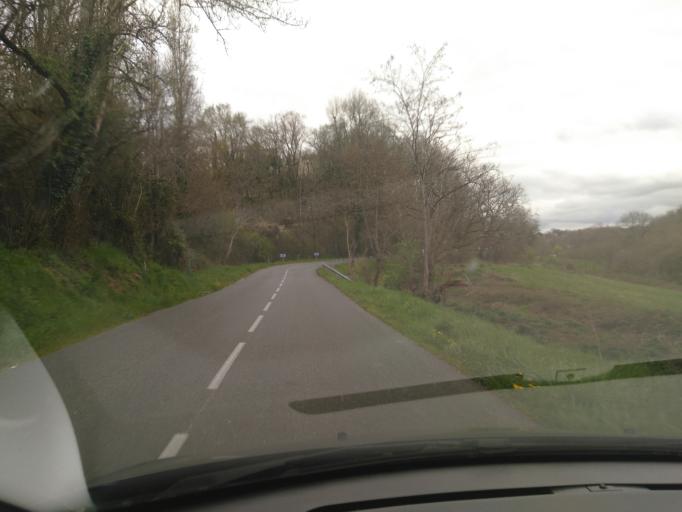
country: FR
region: Aquitaine
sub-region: Departement du Lot-et-Garonne
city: Foulayronnes
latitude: 44.2355
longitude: 0.6355
